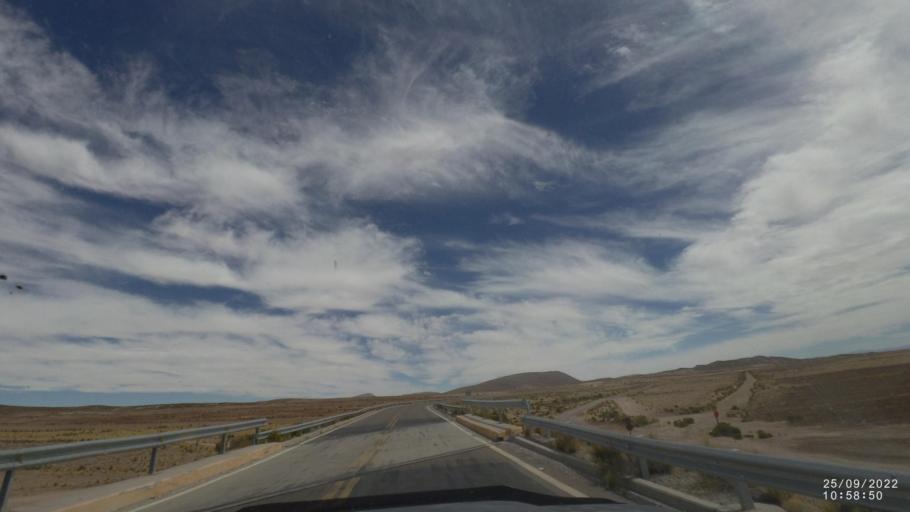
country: BO
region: Oruro
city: Challapata
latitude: -19.4581
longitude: -66.9085
